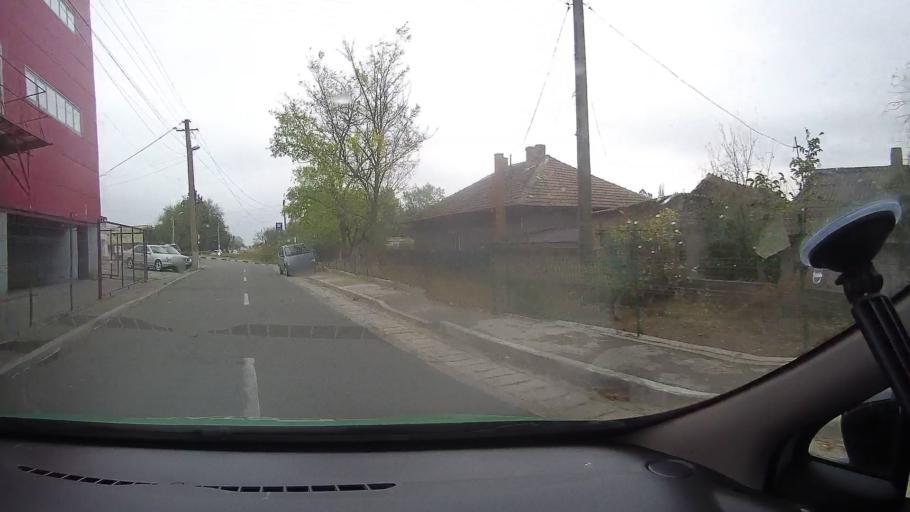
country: RO
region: Constanta
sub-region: Oras Murfatlar
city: Murfatlar
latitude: 44.1729
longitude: 28.4123
